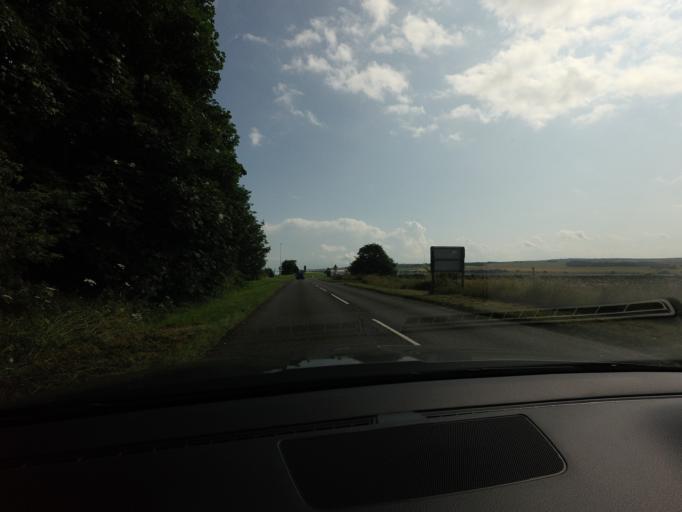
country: GB
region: Scotland
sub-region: Highland
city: Evanton
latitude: 57.6273
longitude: -4.3693
